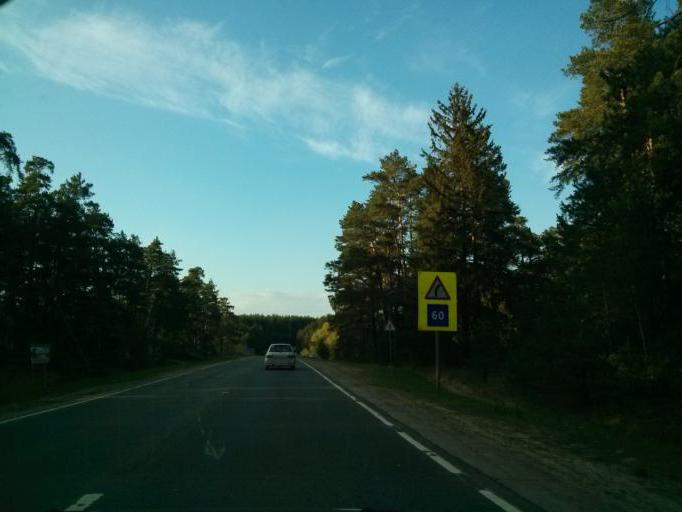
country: RU
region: Nizjnij Novgorod
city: Navashino
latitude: 55.6623
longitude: 42.2590
